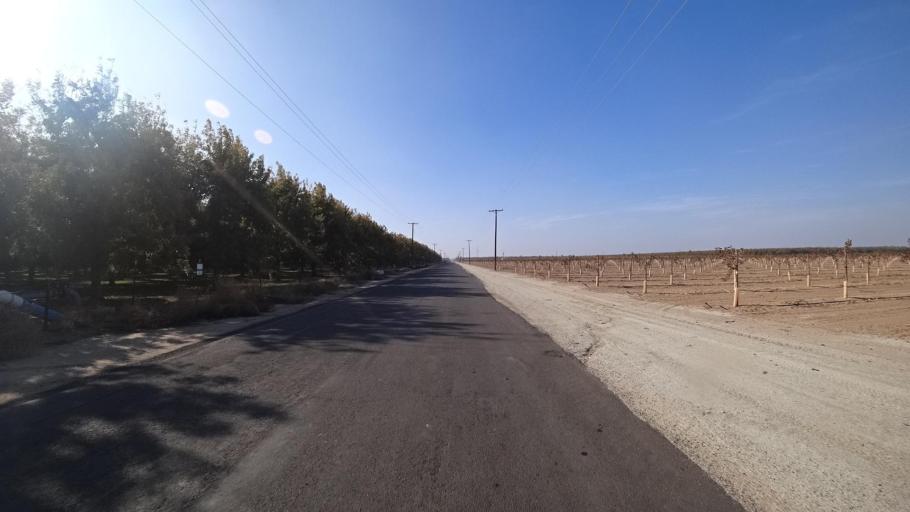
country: US
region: California
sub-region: Kern County
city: McFarland
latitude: 35.6311
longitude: -119.1909
